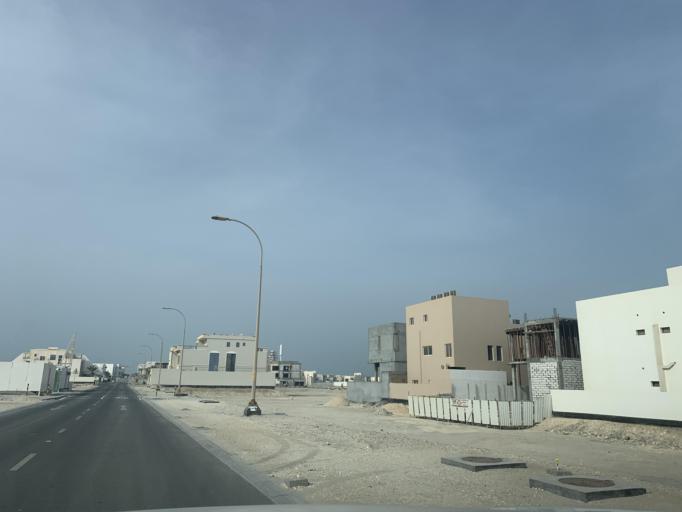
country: BH
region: Muharraq
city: Al Muharraq
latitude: 26.3196
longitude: 50.6220
